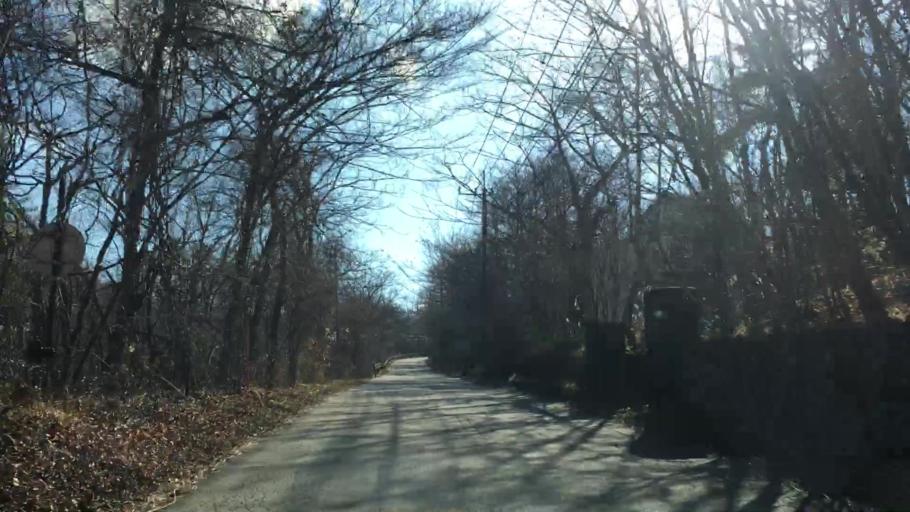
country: JP
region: Shizuoka
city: Gotemba
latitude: 35.3977
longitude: 138.8634
